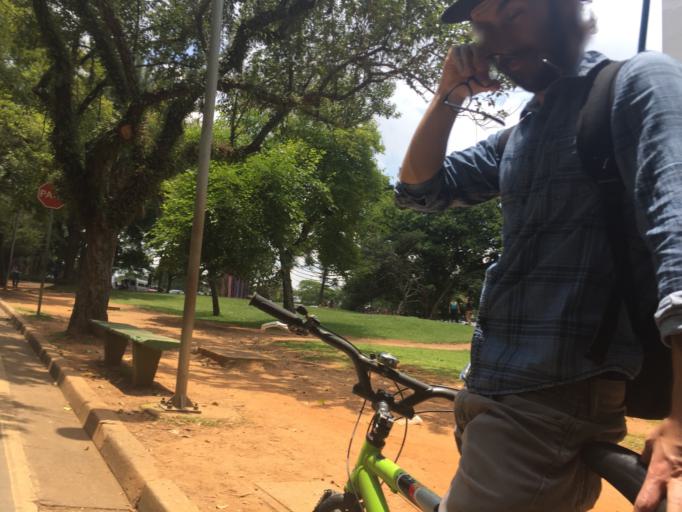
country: BR
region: Sao Paulo
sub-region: Sao Paulo
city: Sao Paulo
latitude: -23.5892
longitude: -46.6558
